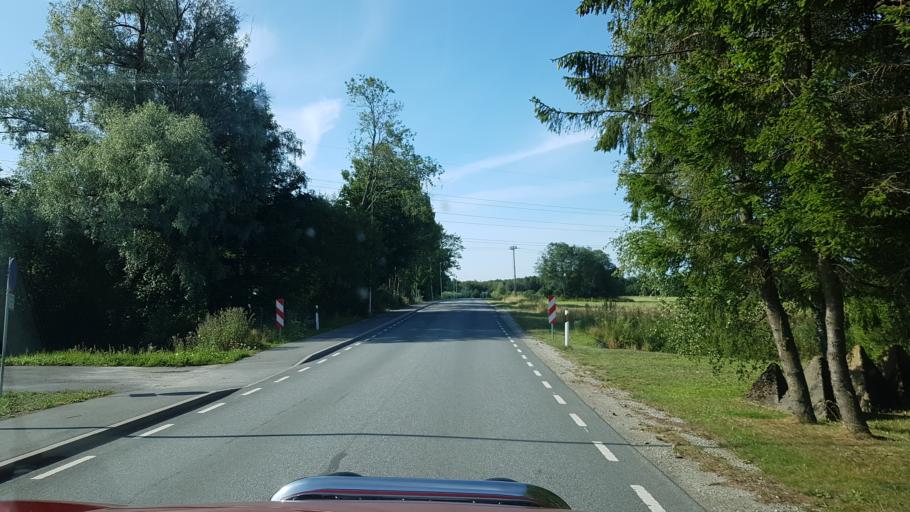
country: EE
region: Harju
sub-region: Joelaehtme vald
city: Loo
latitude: 59.3878
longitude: 24.9349
